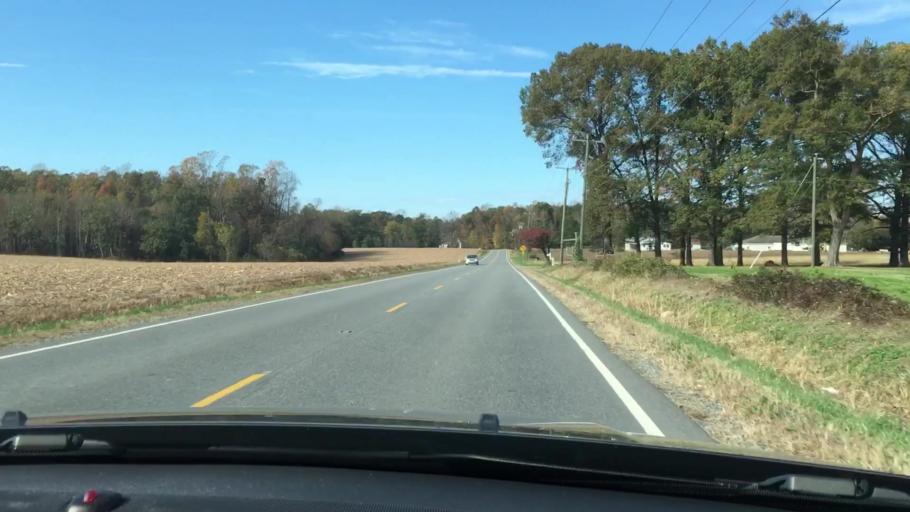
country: US
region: Virginia
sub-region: King William County
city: West Point
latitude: 37.5872
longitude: -76.8547
